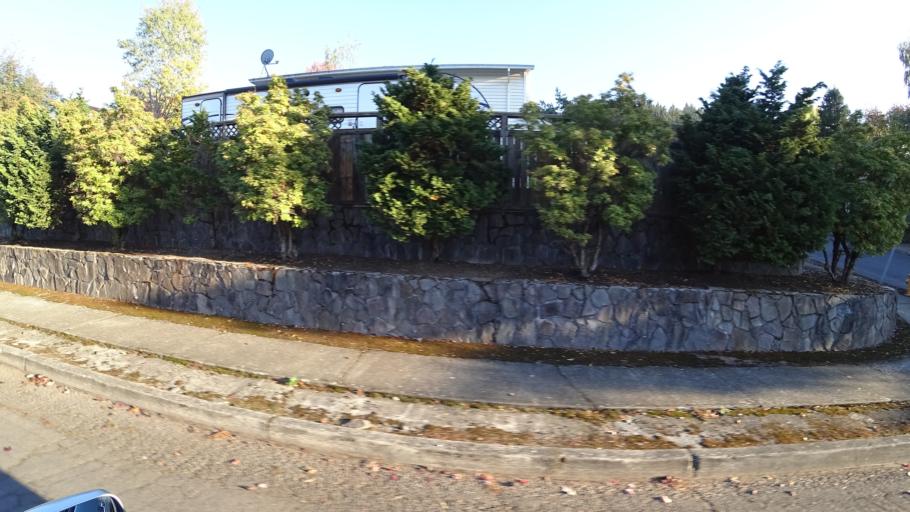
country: US
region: Oregon
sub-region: Multnomah County
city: Gresham
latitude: 45.4928
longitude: -122.4418
